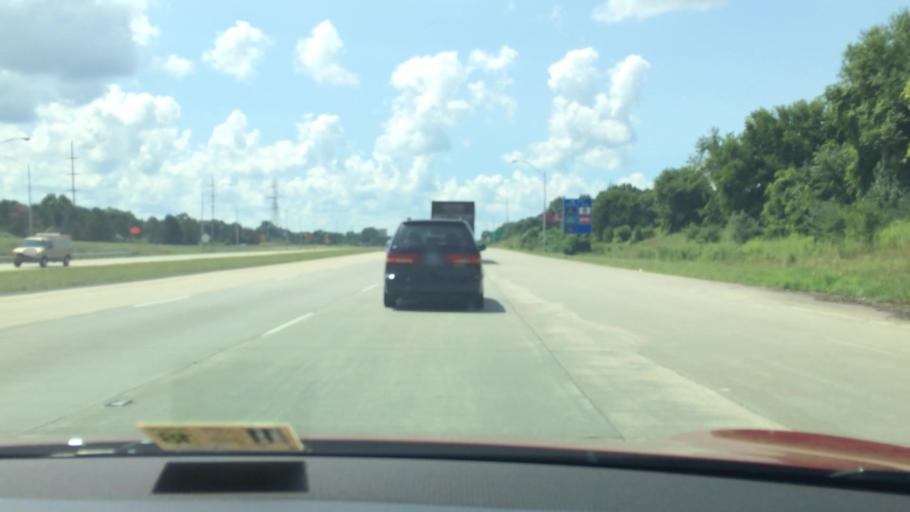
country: US
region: Indiana
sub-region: Saint Joseph County
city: South Bend
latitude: 41.7225
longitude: -86.3397
